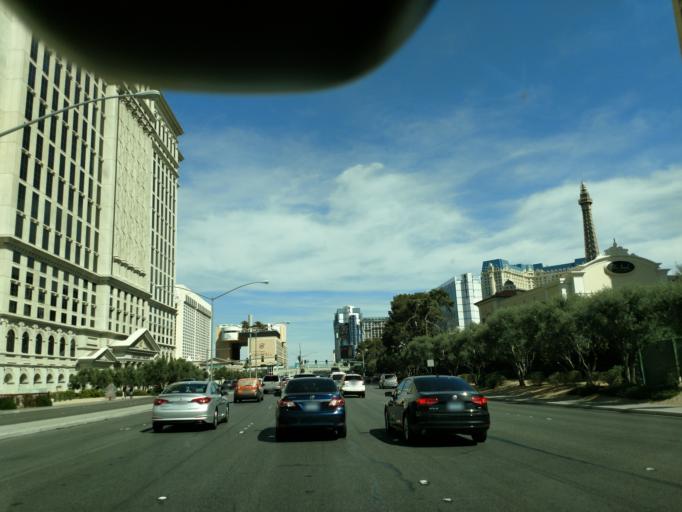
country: US
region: Nevada
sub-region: Clark County
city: Paradise
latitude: 36.1147
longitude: -115.1770
